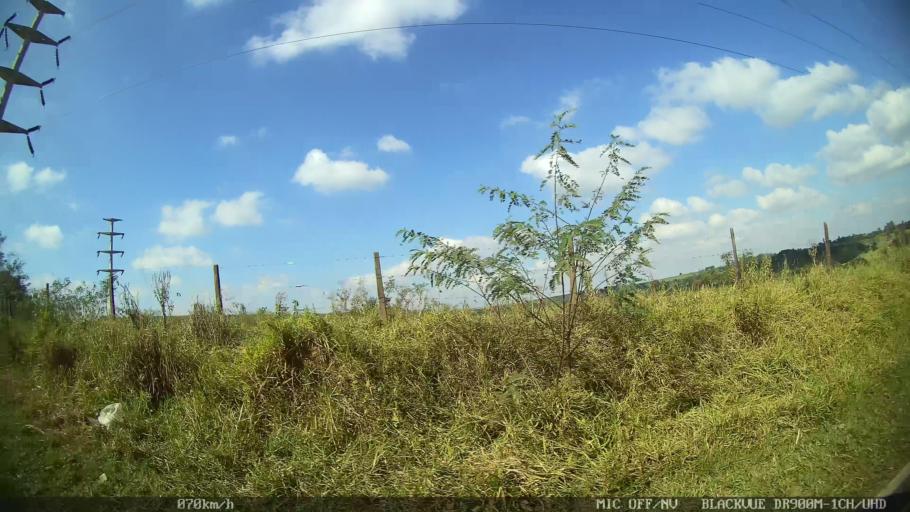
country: BR
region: Sao Paulo
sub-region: Indaiatuba
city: Indaiatuba
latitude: -22.9925
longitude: -47.1753
